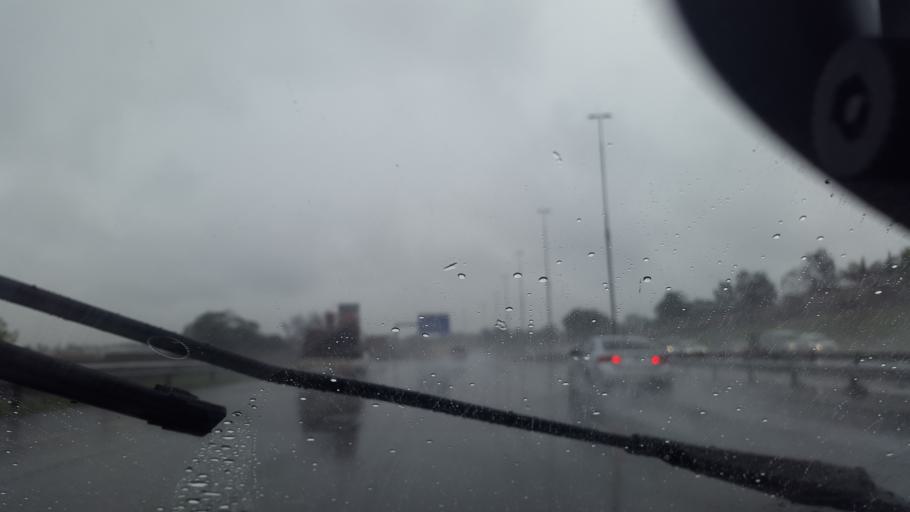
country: ZA
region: Gauteng
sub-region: City of Johannesburg Metropolitan Municipality
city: Johannesburg
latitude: -26.2630
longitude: 28.0173
